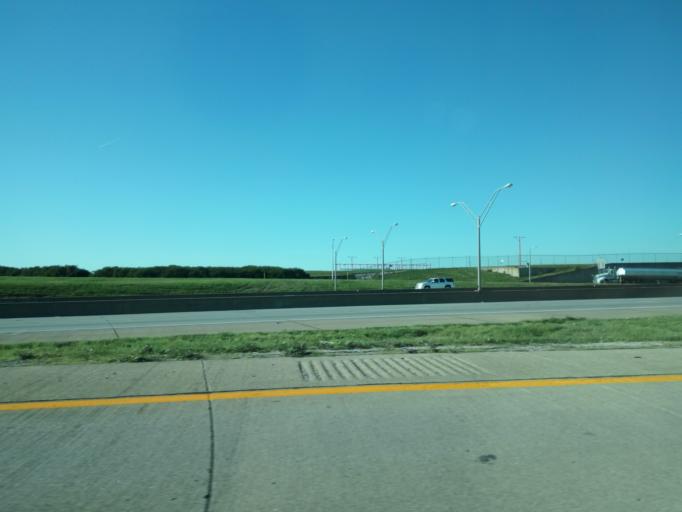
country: US
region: Kentucky
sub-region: Jefferson County
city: Audubon Park
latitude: 38.1905
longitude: -85.7315
